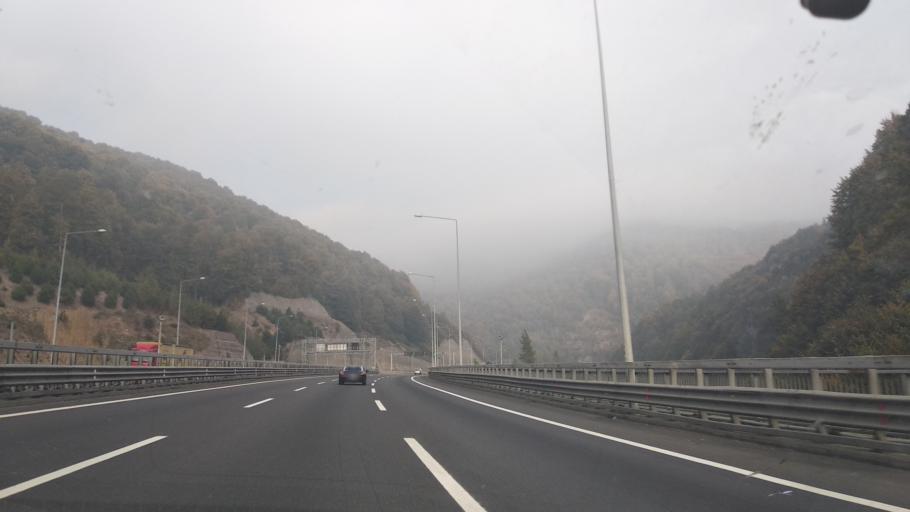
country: TR
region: Duzce
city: Kaynasli
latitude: 40.7581
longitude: 31.4418
